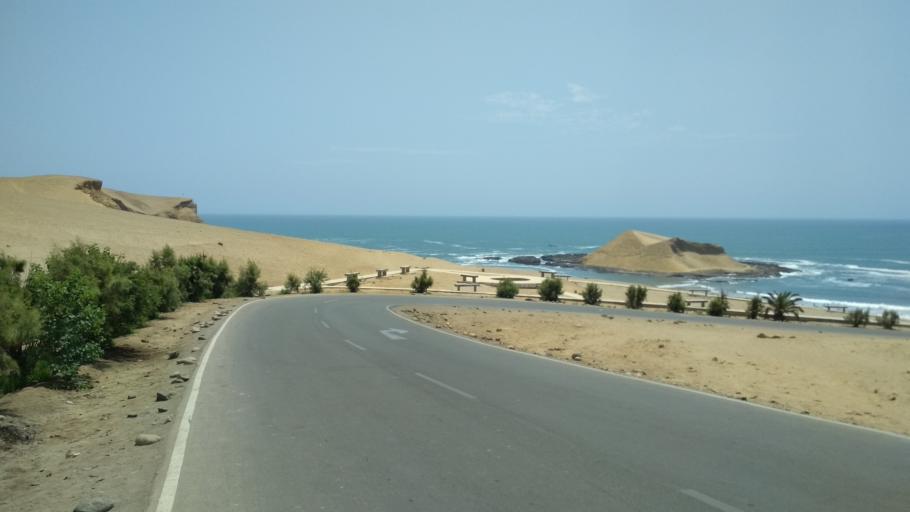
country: PE
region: Lima
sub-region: Barranca
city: Puerto Supe
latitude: -10.8089
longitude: -77.7477
